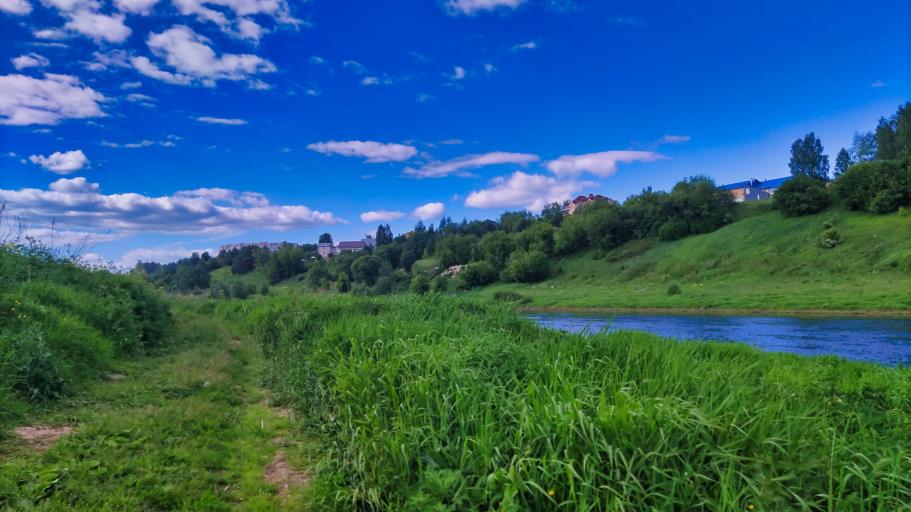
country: RU
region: Tverskaya
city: Rzhev
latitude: 56.2498
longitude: 34.3487
